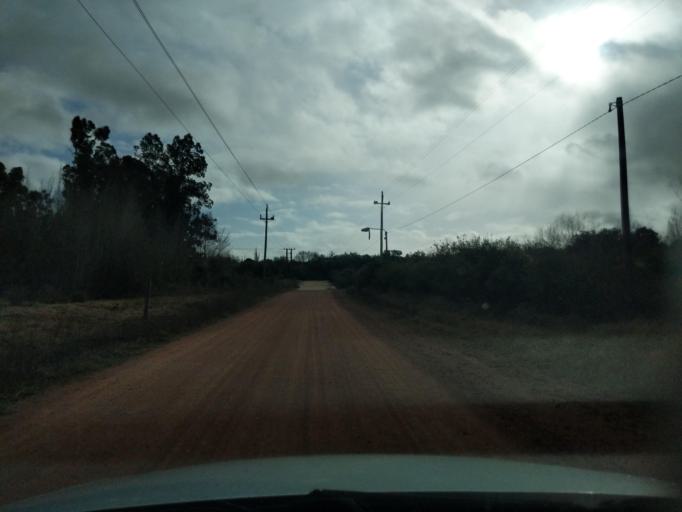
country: UY
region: Florida
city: Florida
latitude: -34.0602
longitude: -56.2163
